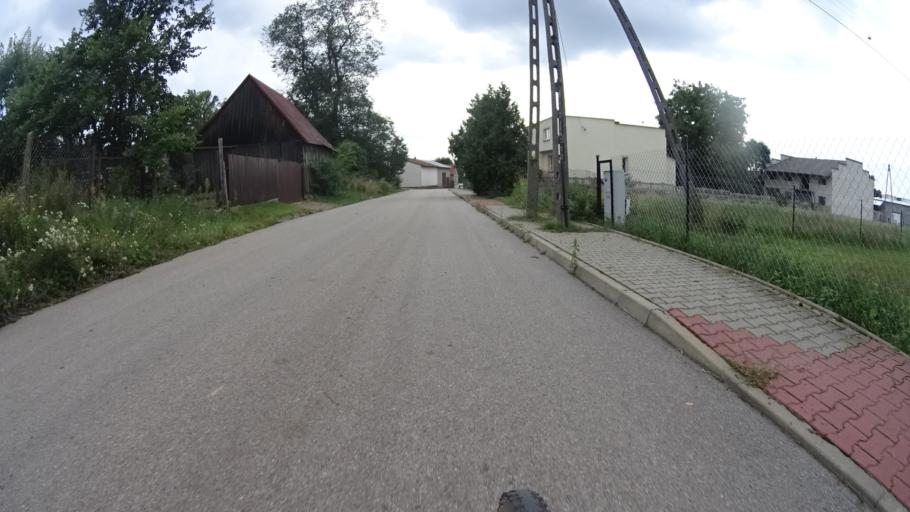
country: PL
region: Masovian Voivodeship
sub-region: Powiat bialobrzeski
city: Wysmierzyce
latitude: 51.6642
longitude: 20.8513
